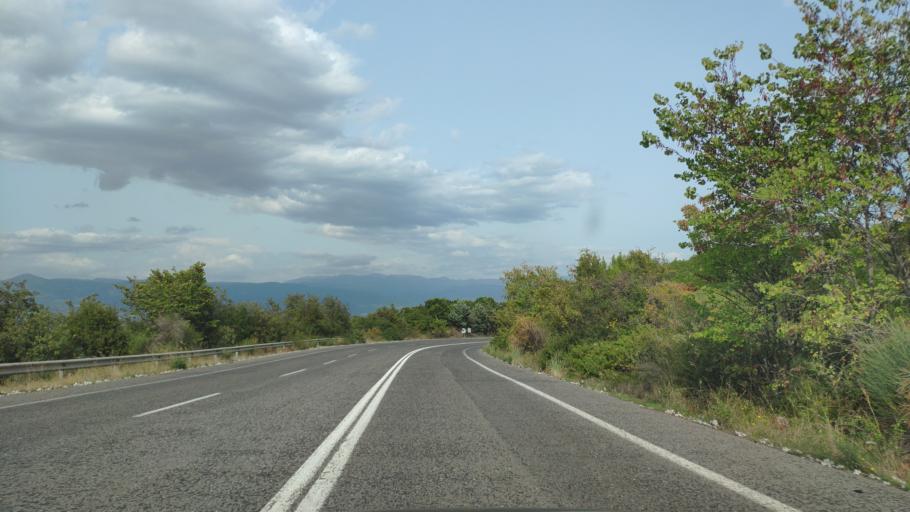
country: GR
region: Central Greece
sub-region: Nomos Fthiotidos
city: Anthili
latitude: 38.7993
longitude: 22.4883
